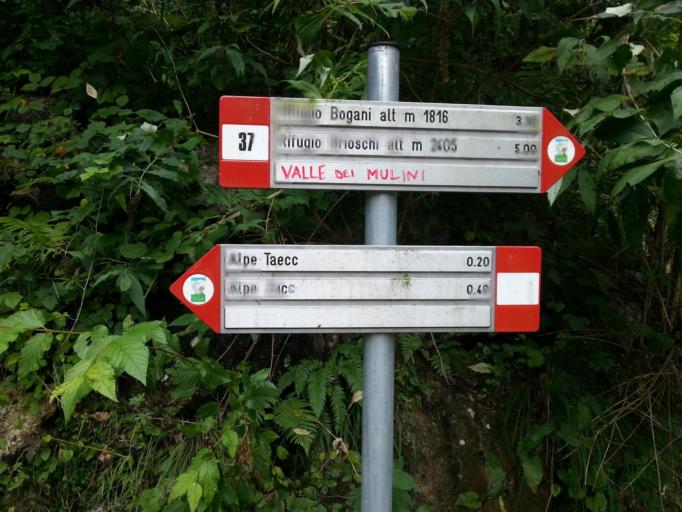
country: IT
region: Lombardy
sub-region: Provincia di Lecco
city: Cortenova
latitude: 45.9908
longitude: 9.3836
